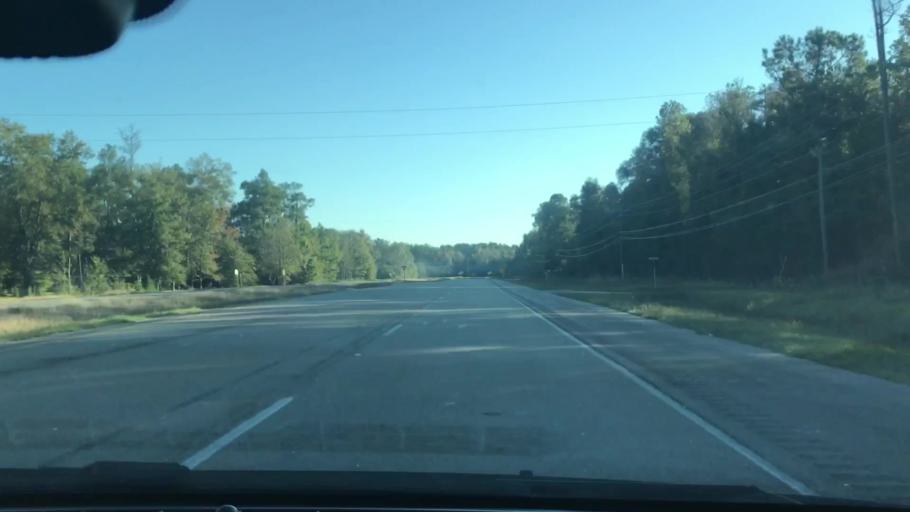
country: US
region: Louisiana
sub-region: Washington Parish
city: Bogalusa
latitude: 30.6150
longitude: -89.8990
